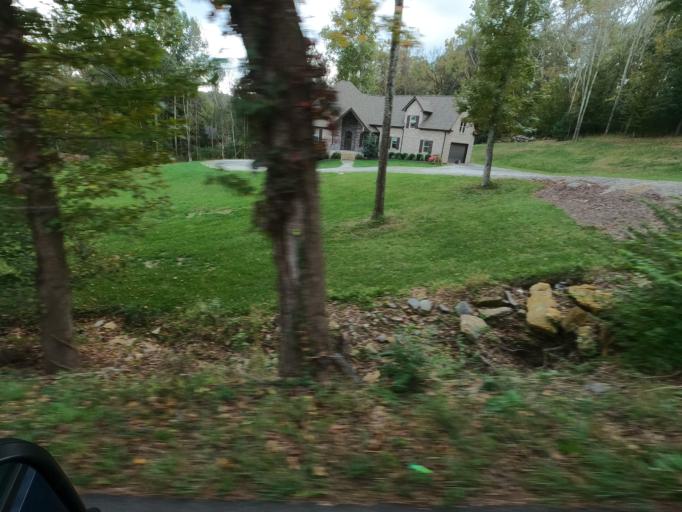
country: US
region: Tennessee
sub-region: Cheatham County
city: Pegram
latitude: 36.1060
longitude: -87.0821
